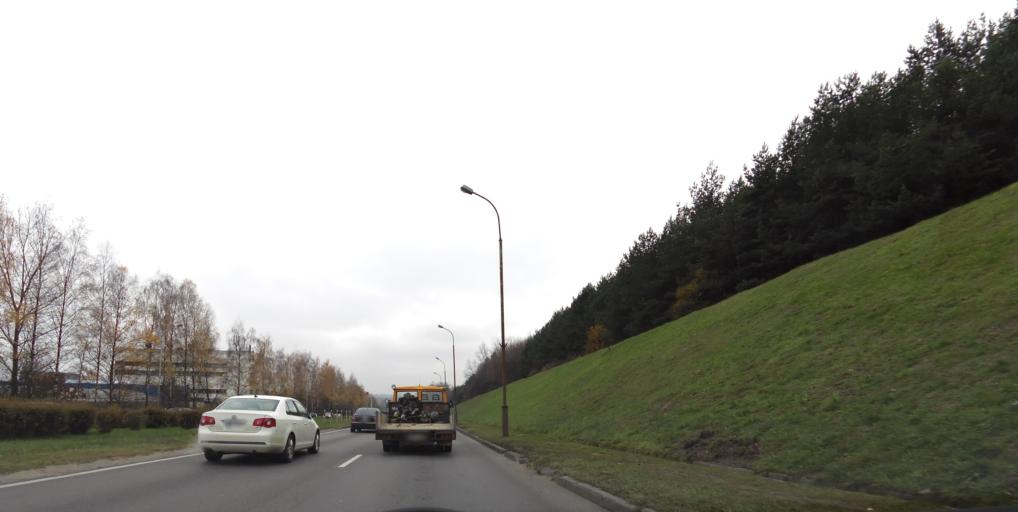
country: LT
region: Vilnius County
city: Seskine
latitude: 54.7098
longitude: 25.2689
